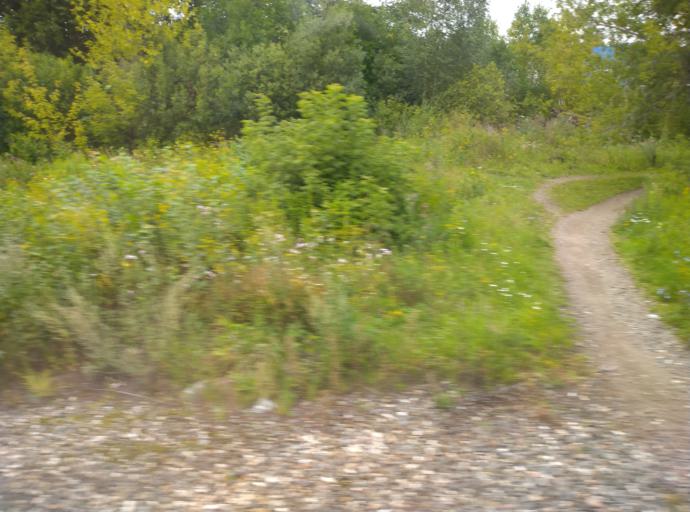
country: RU
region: Jaroslavl
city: Yaroslavl
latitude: 57.5898
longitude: 39.8885
